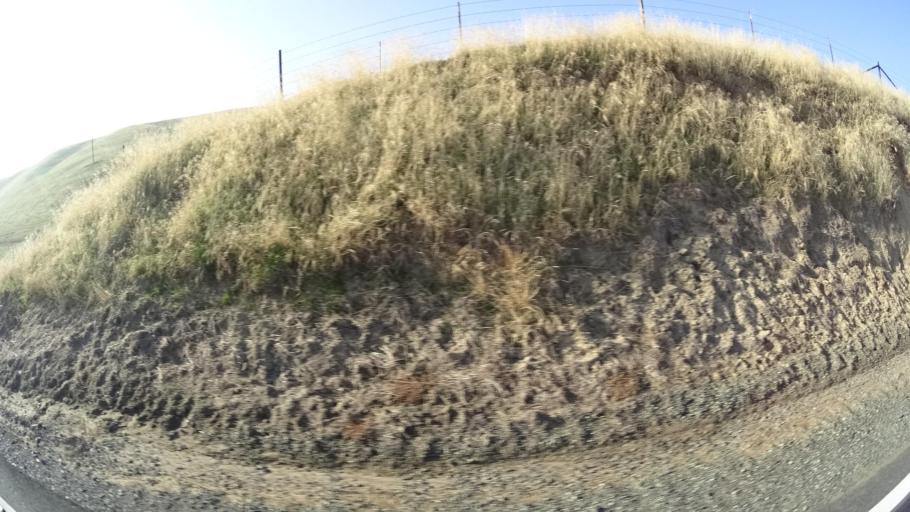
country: US
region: California
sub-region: Tulare County
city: Richgrove
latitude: 35.7475
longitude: -118.9834
